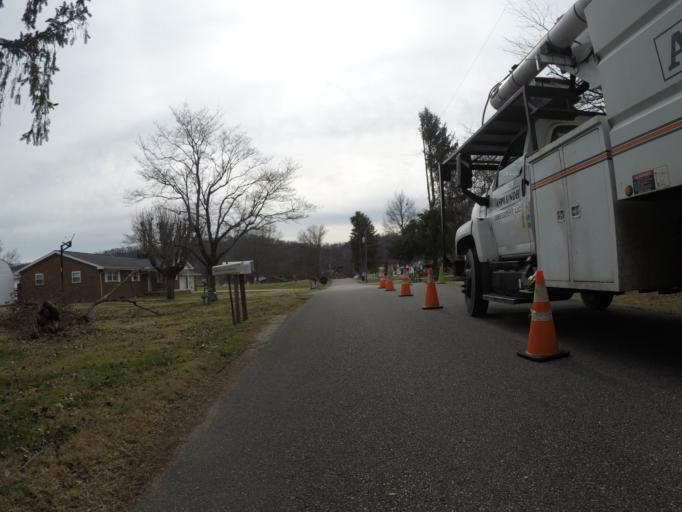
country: US
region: West Virginia
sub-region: Cabell County
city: Pea Ridge
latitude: 38.4446
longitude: -82.3460
